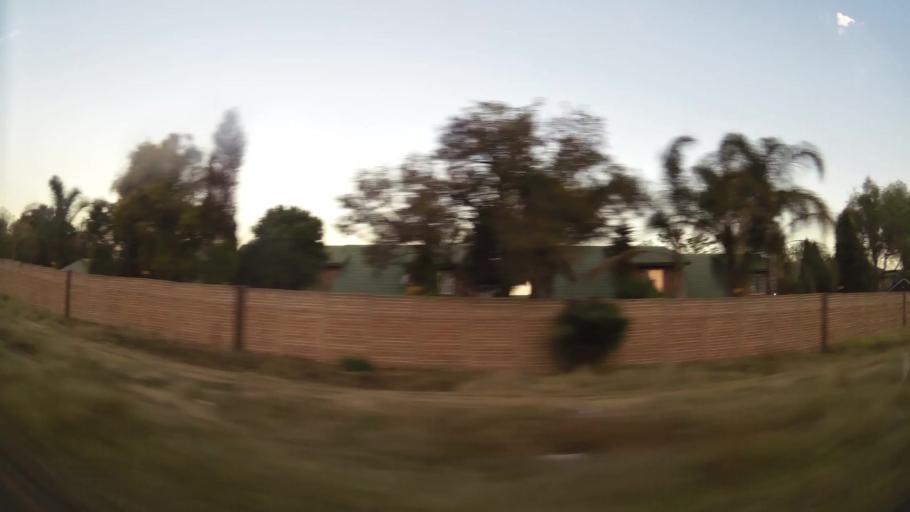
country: ZA
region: Gauteng
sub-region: City of Tshwane Metropolitan Municipality
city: Centurion
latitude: -25.8600
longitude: 28.1366
